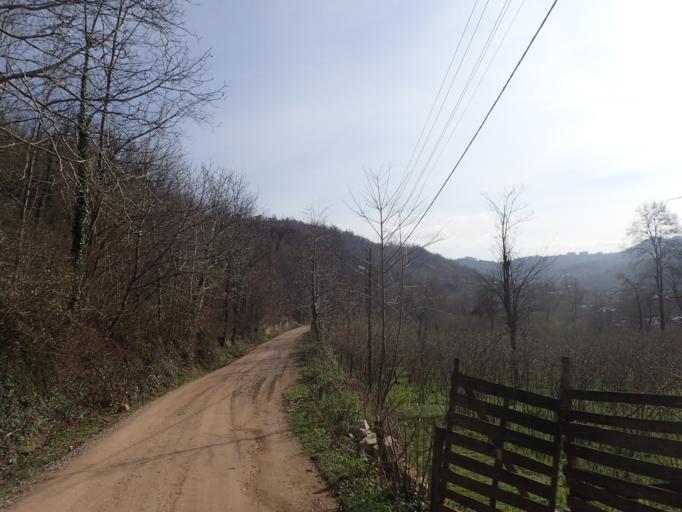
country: TR
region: Ordu
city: Camas
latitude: 40.9418
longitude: 37.5138
